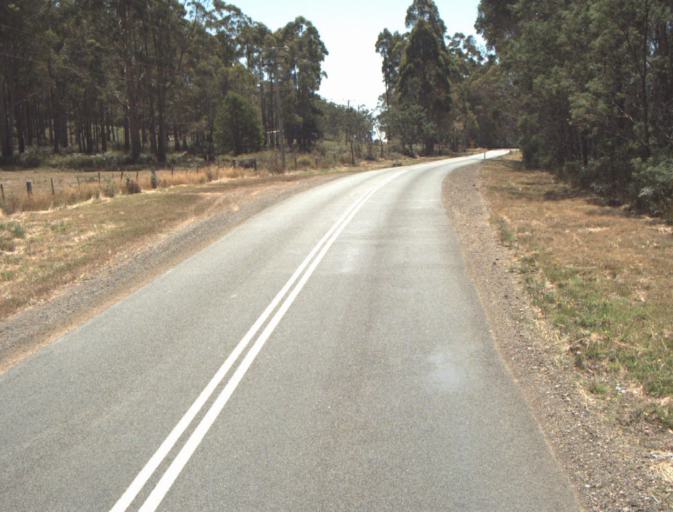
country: AU
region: Tasmania
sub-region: Launceston
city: Mayfield
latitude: -41.2817
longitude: 147.1261
